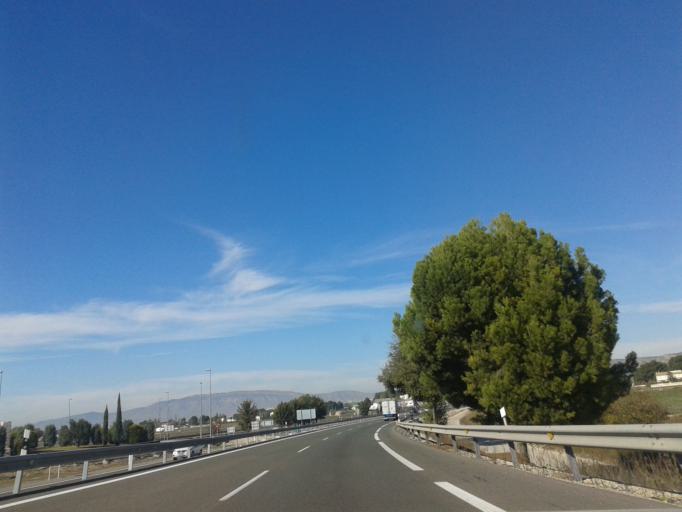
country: ES
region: Valencia
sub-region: Provincia de Alicante
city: Villena
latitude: 38.6496
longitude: -0.8713
